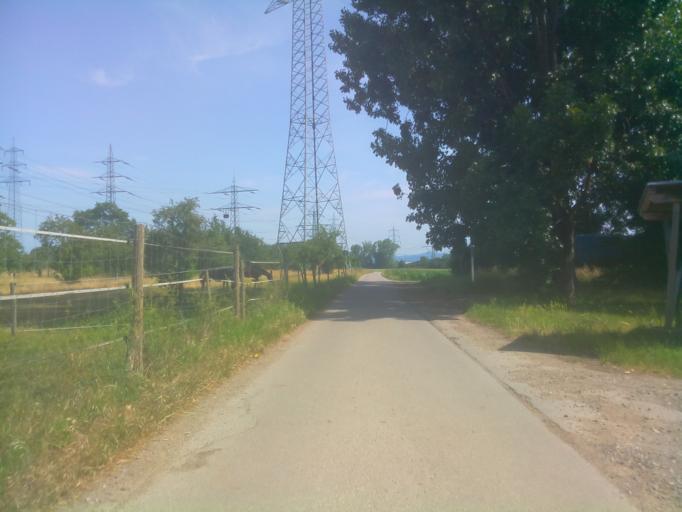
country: DE
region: Baden-Wuerttemberg
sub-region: Karlsruhe Region
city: Heddesheim
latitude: 49.5384
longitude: 8.6207
